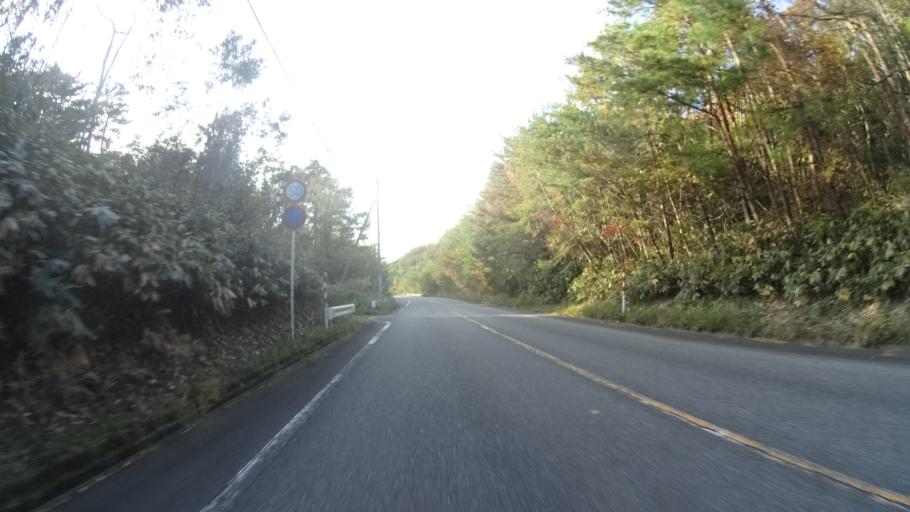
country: JP
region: Ishikawa
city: Hakui
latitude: 37.0701
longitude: 136.7458
